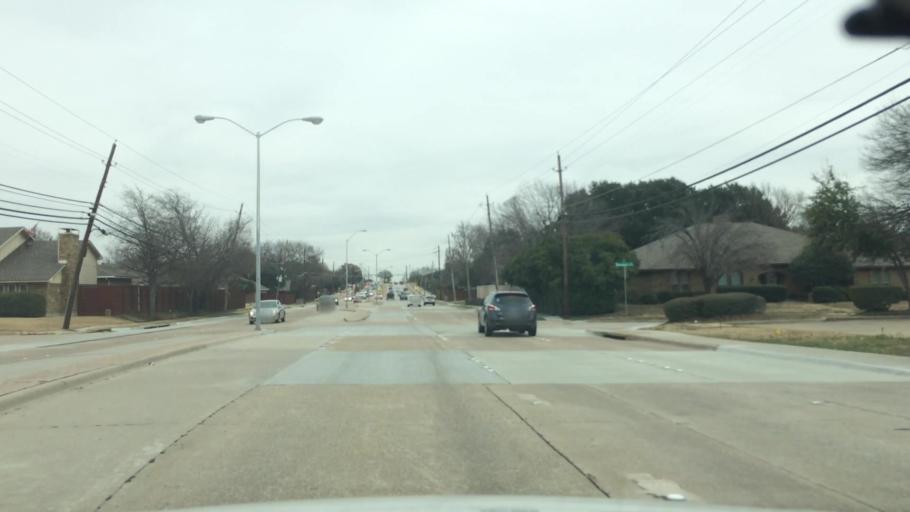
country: US
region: Texas
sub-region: Collin County
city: Plano
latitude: 33.0410
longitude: -96.7499
